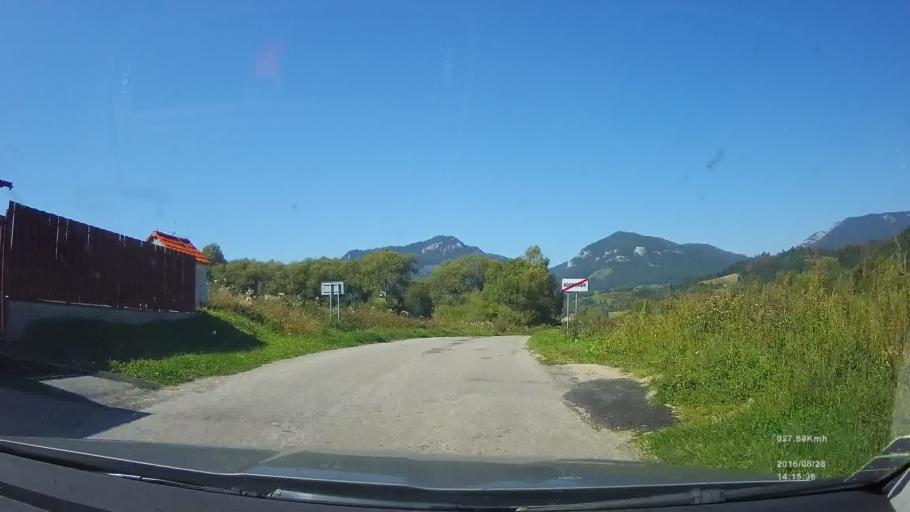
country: SK
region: Zilinsky
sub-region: Okres Liptovsky Mikulas
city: Liptovsky Mikulas
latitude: 49.1202
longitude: 19.4780
